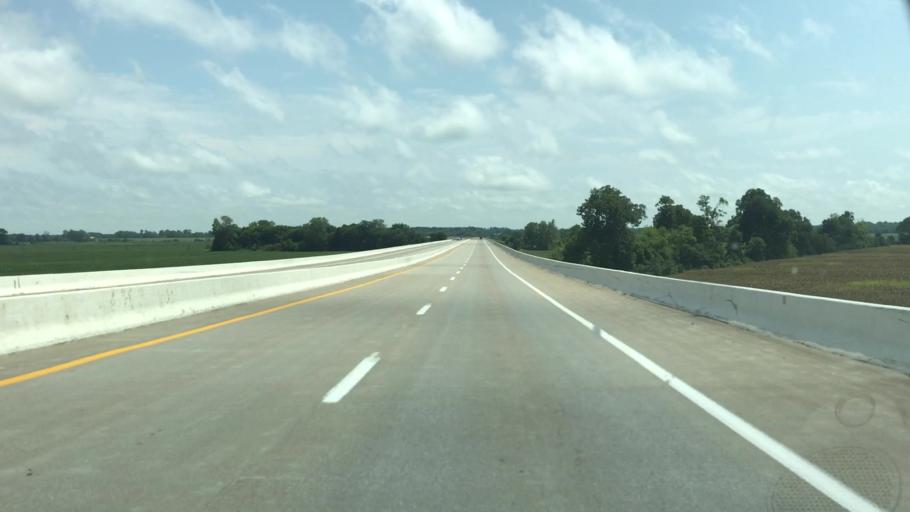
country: US
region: Missouri
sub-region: Pemiscot County
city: Caruthersville
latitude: 36.1078
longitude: -89.6090
